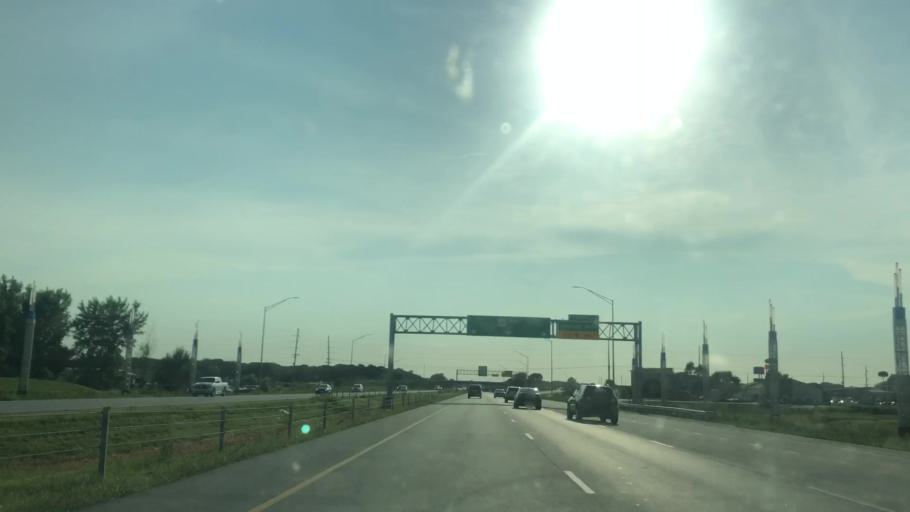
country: US
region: Iowa
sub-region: Story County
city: Ames
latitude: 42.0073
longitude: -93.5780
